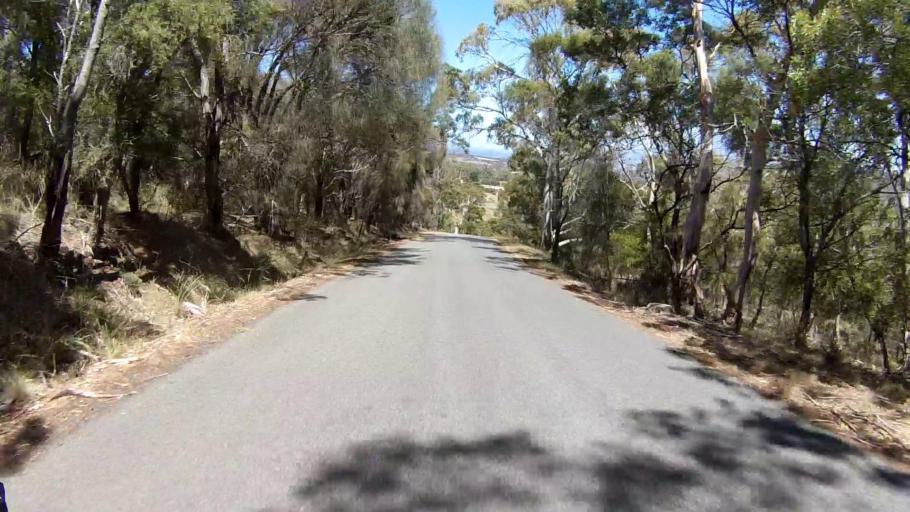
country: AU
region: Tasmania
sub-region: Clarence
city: Cambridge
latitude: -42.8500
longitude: 147.4299
